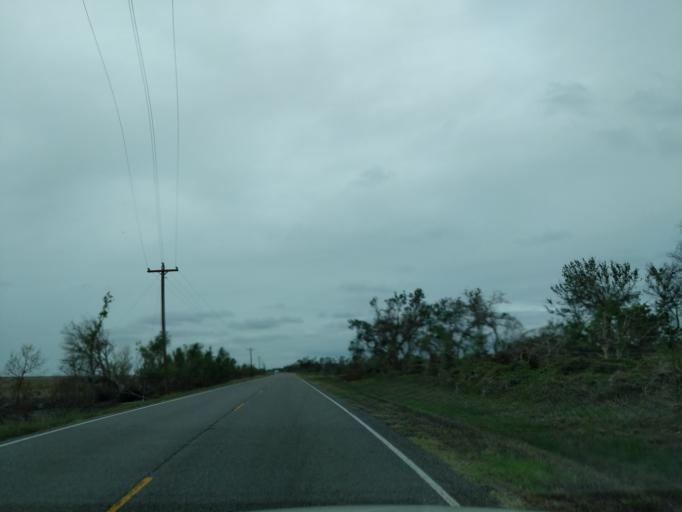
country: US
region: Louisiana
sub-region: Cameron Parish
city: Cameron
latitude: 29.7867
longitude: -93.1443
